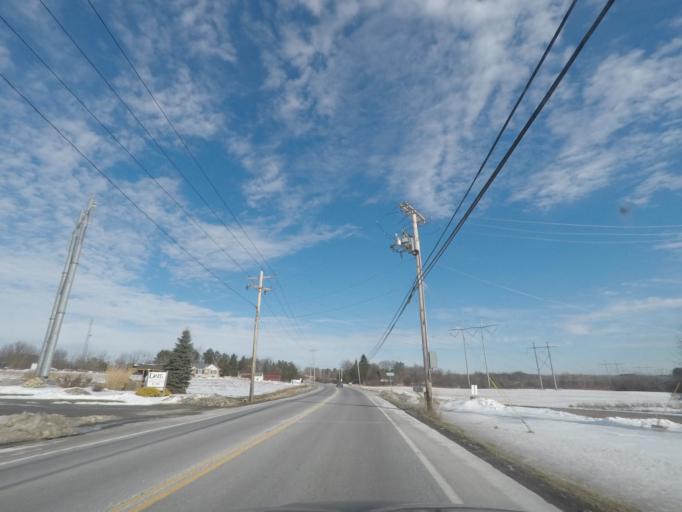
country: US
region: New York
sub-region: Schenectady County
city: Rotterdam
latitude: 42.7783
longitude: -74.0374
